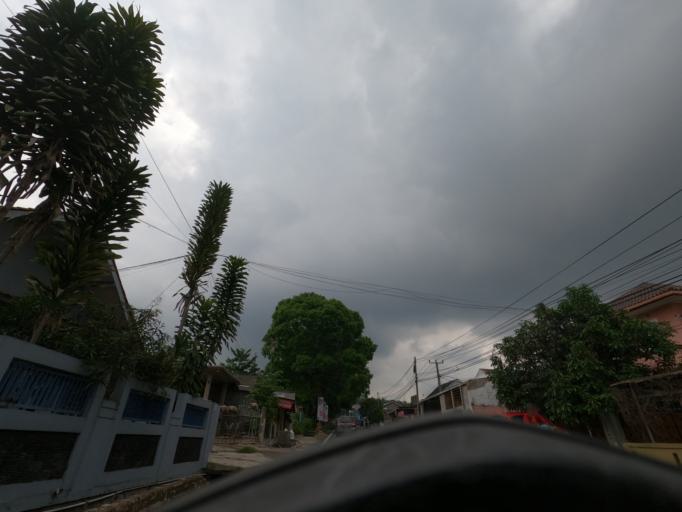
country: ID
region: West Java
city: Sukabumi
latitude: -6.7632
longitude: 107.0525
